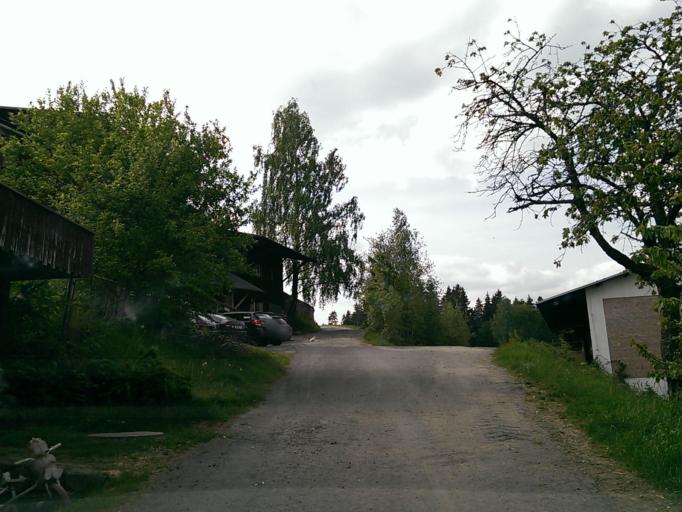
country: CZ
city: Plavy
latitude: 50.7008
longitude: 15.3104
